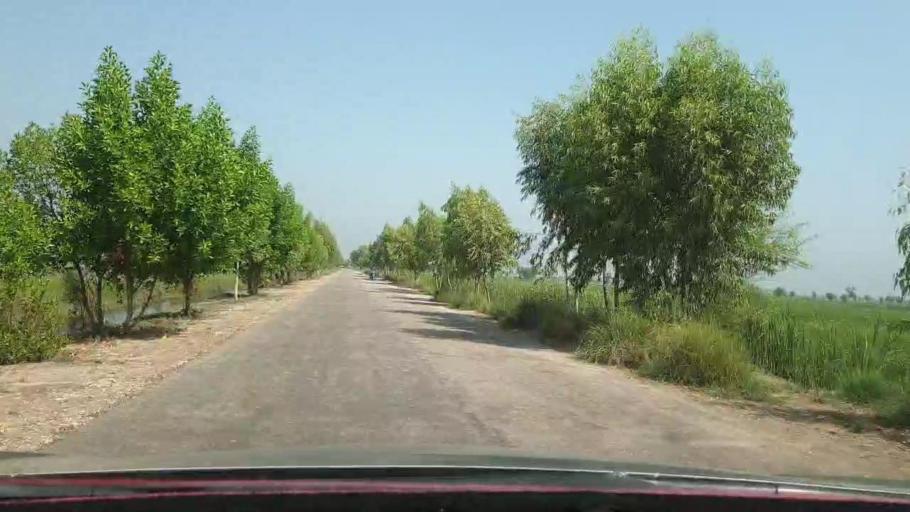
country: PK
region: Sindh
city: Warah
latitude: 27.4678
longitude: 67.8337
